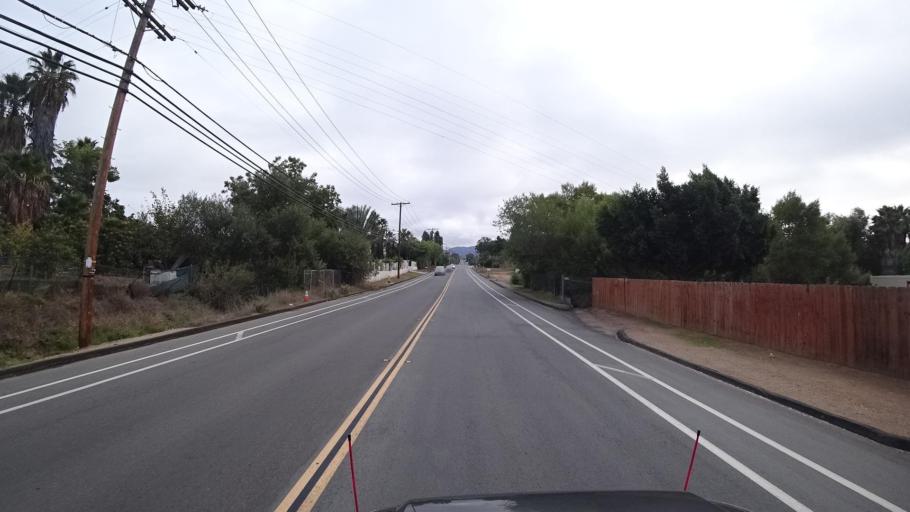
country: US
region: California
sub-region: San Diego County
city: Rancho San Diego
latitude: 32.7621
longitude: -116.9256
